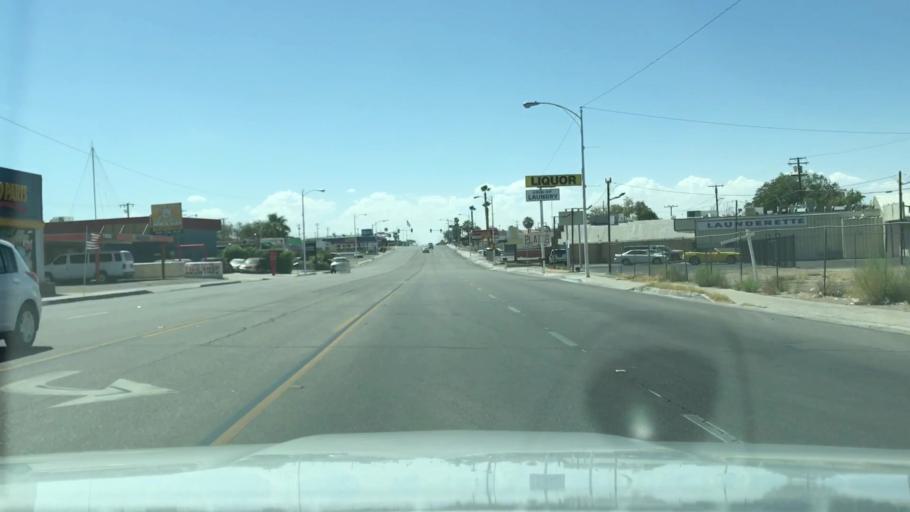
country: US
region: California
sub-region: San Bernardino County
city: Barstow
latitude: 34.8949
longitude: -117.0444
